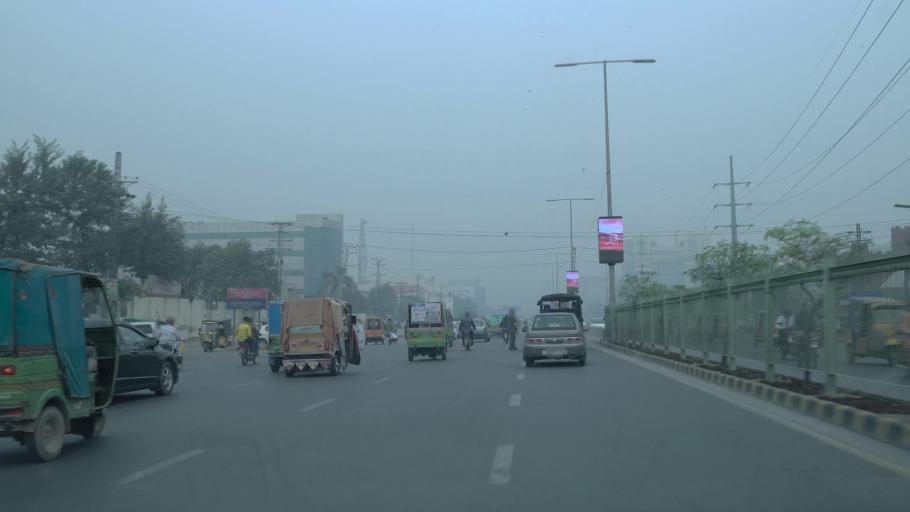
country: PK
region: Punjab
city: Lahore
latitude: 31.5015
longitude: 74.3217
